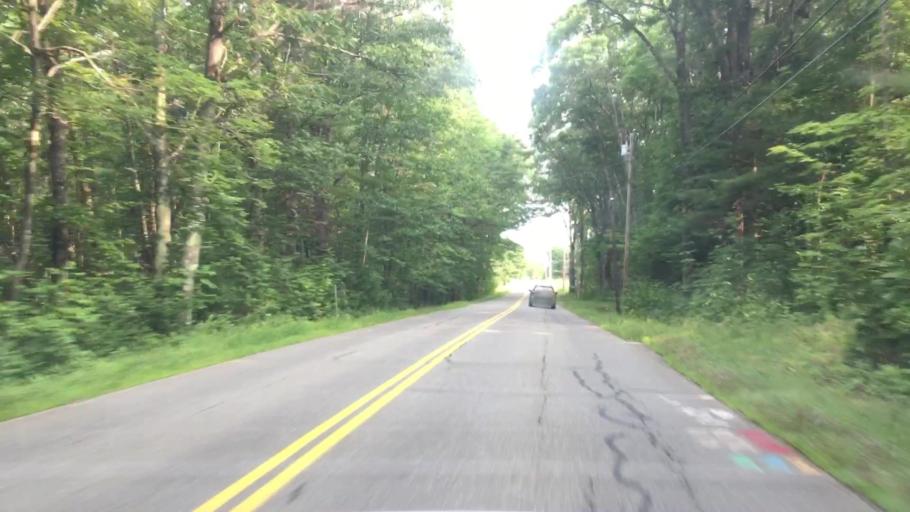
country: US
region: Maine
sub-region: Kennebec County
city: Chelsea
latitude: 44.2971
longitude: -69.6971
